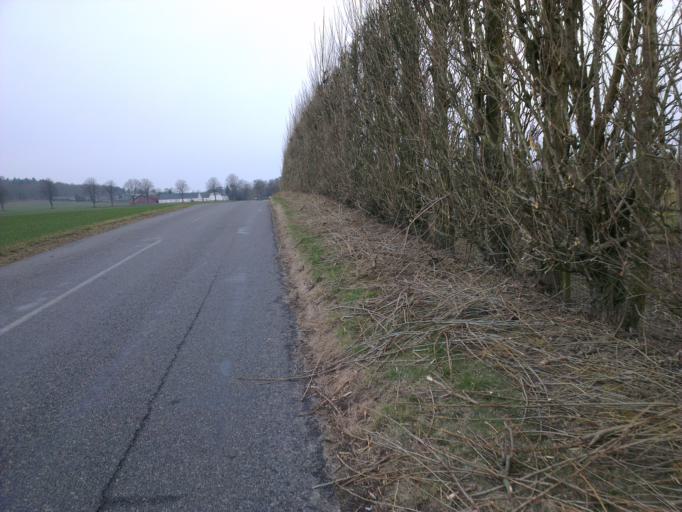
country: DK
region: Capital Region
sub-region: Frederikssund Kommune
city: Skibby
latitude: 55.7926
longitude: 11.9661
